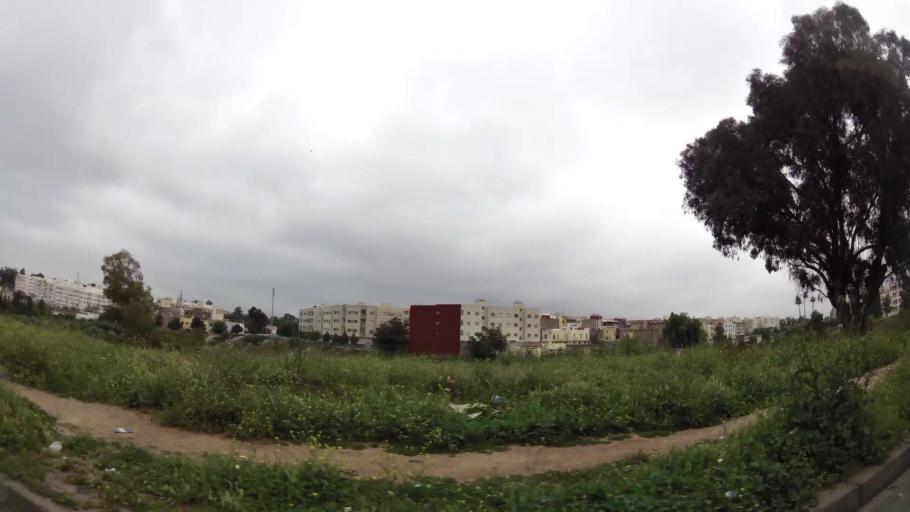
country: MA
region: Fes-Boulemane
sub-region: Fes
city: Fes
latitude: 34.0363
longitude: -4.9928
